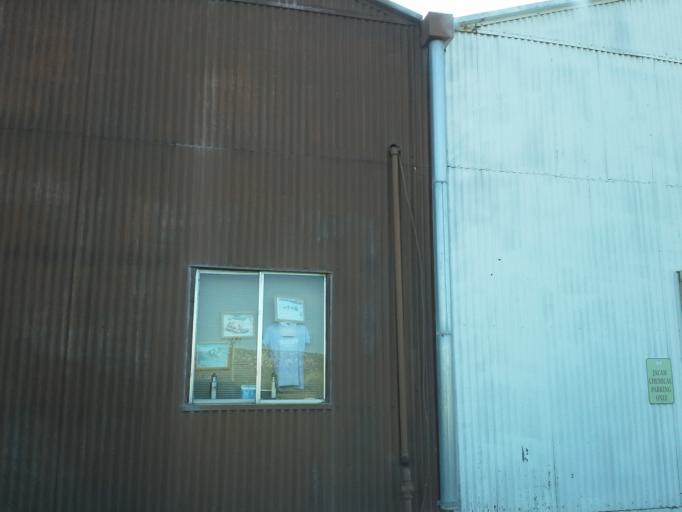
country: US
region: Wyoming
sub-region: Hot Springs County
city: Thermopolis
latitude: 43.6227
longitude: -108.2219
